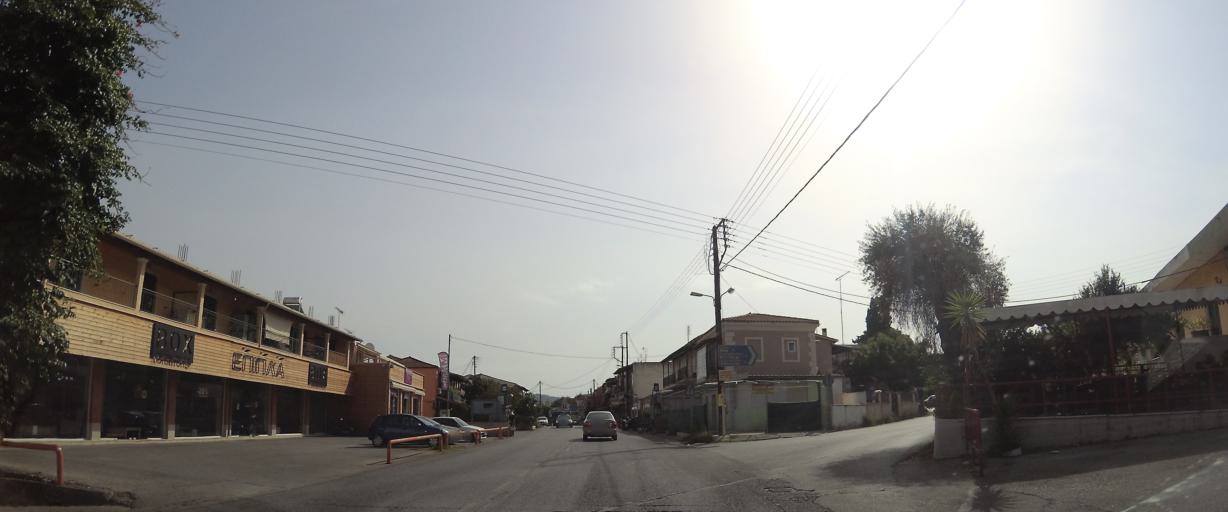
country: GR
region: Ionian Islands
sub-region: Nomos Kerkyras
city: Kanali
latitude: 39.5926
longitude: 19.8926
